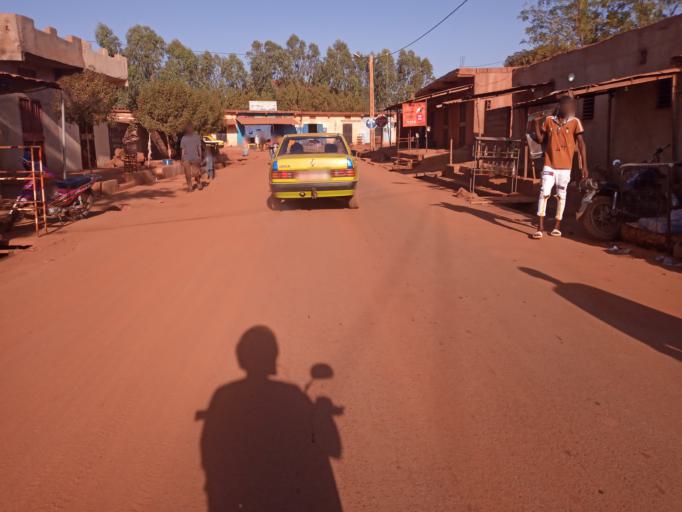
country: ML
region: Bamako
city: Bamako
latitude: 12.6149
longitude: -7.9487
